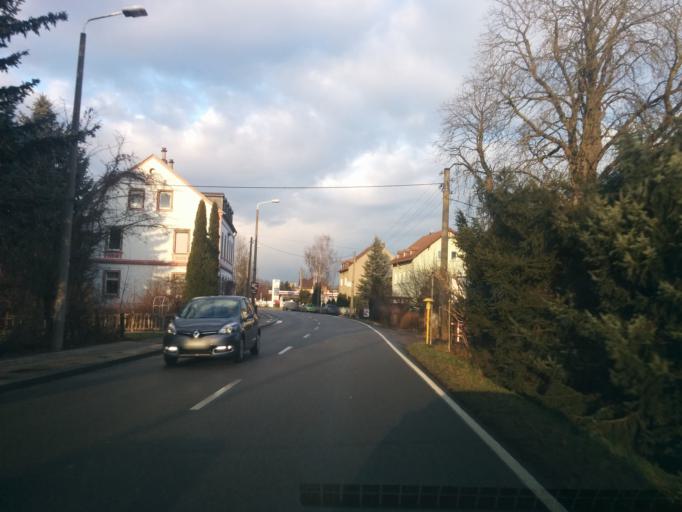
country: DE
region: Saxony
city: Frankenberg
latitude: 50.9049
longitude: 13.0199
